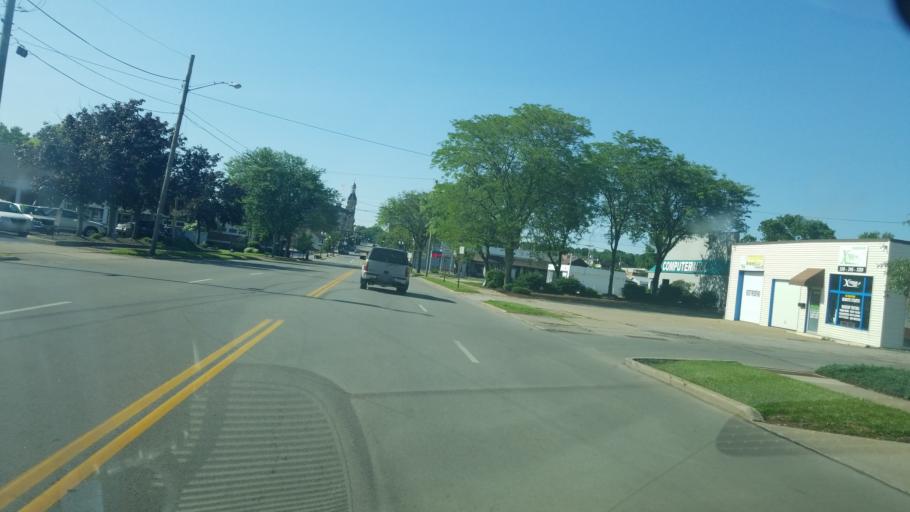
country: US
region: Ohio
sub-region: Wayne County
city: Wooster
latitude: 40.7946
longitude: -81.9390
